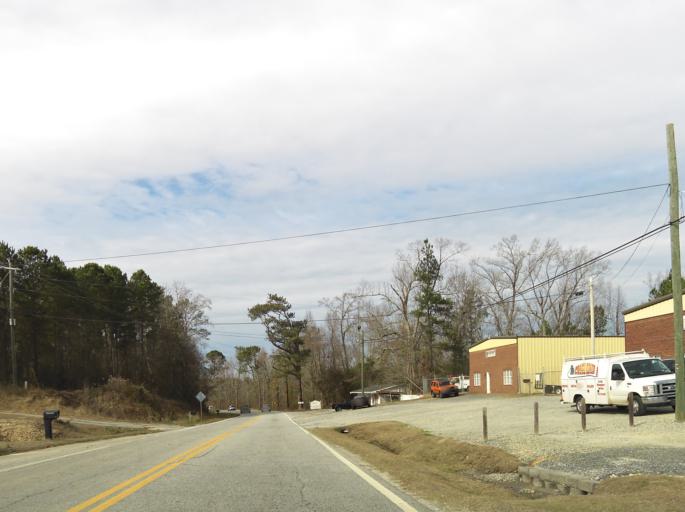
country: US
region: Georgia
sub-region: Bibb County
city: West Point
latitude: 32.8108
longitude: -83.7496
